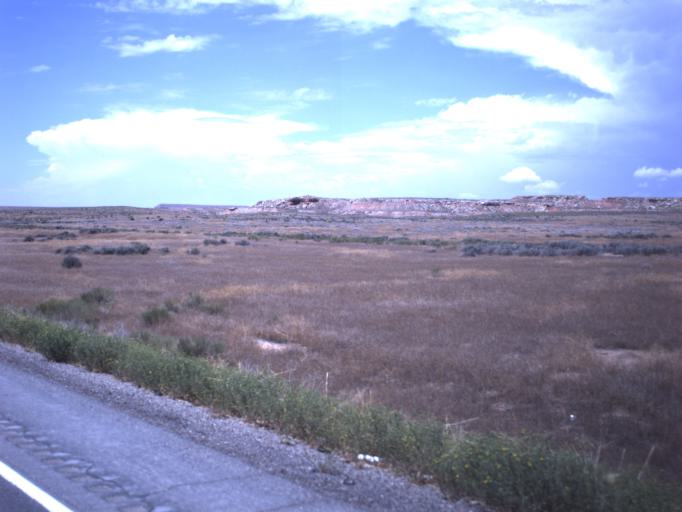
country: US
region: Utah
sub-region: Uintah County
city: Maeser
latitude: 40.3304
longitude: -109.6601
